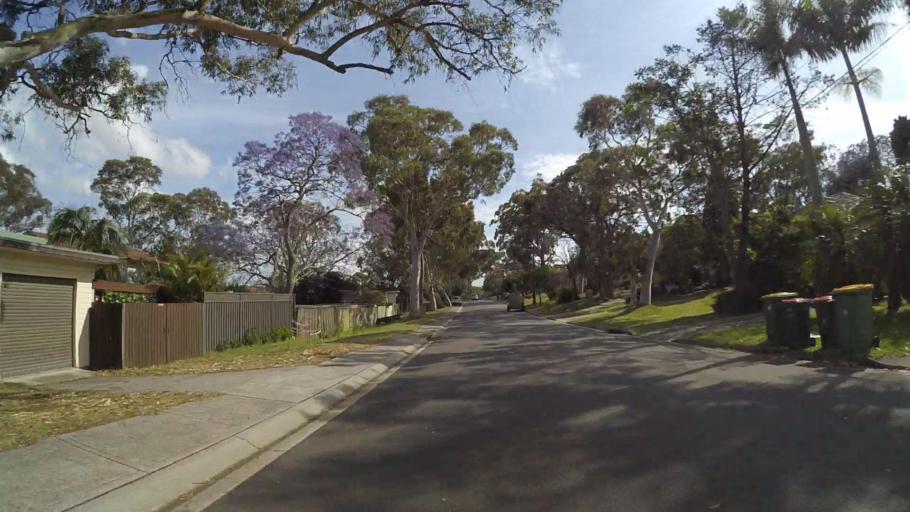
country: AU
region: New South Wales
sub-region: Sutherland Shire
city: Caringbah
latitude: -34.0447
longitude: 151.1151
